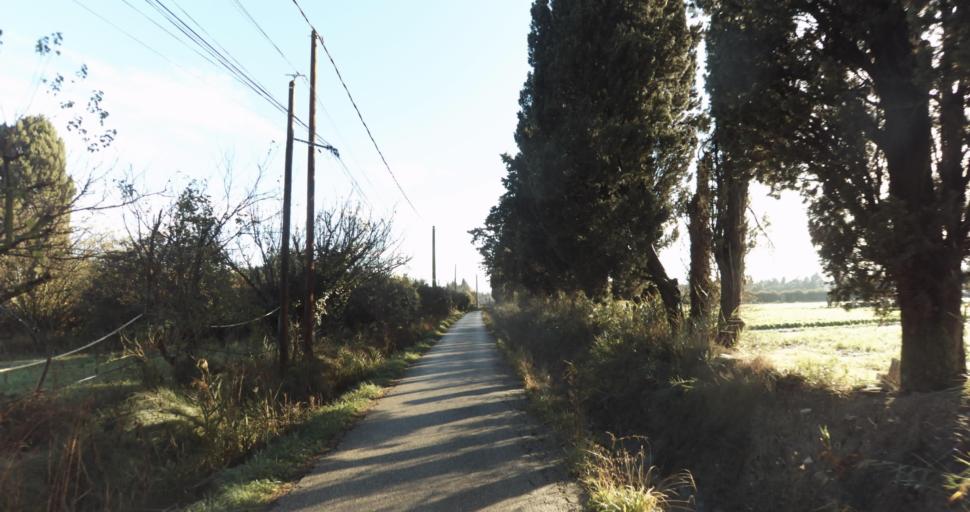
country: FR
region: Provence-Alpes-Cote d'Azur
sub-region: Departement des Bouches-du-Rhone
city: Rognonas
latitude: 43.8837
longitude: 4.7947
